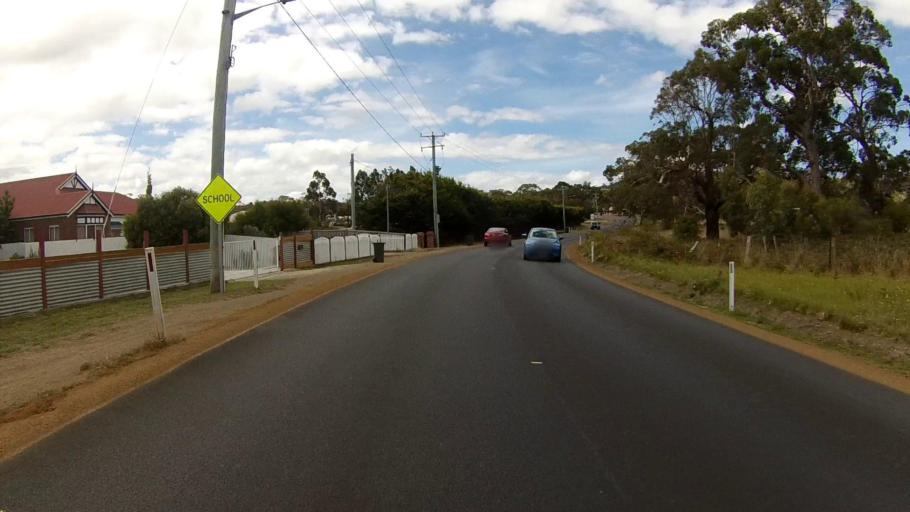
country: AU
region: Tasmania
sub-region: Sorell
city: Sorell
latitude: -42.8509
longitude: 147.6231
